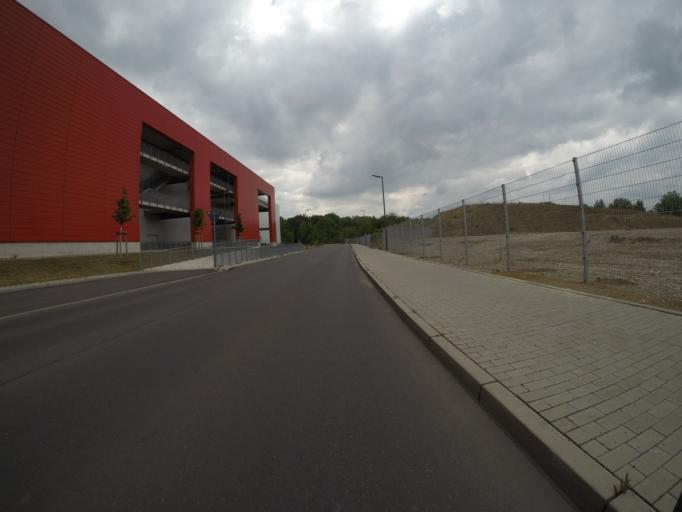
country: DE
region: Berlin
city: Alt-Hohenschoenhausen
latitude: 52.5333
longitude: 13.5046
